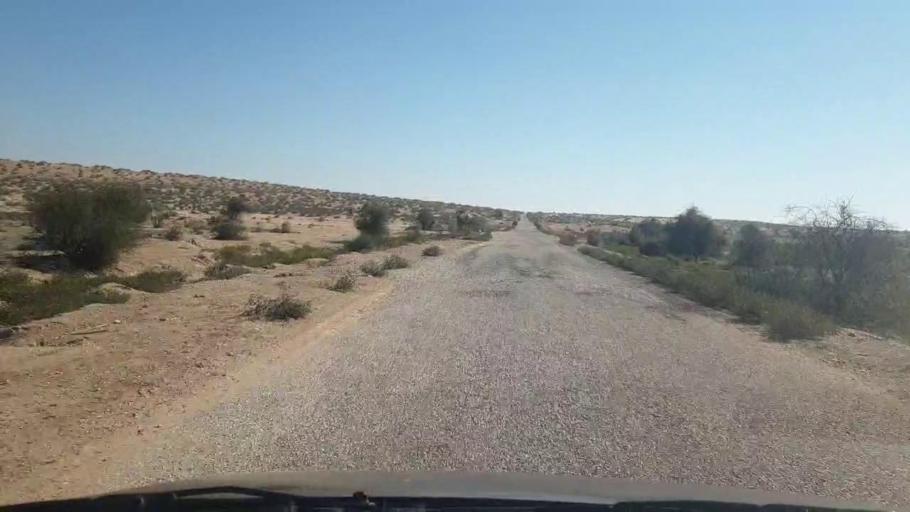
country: PK
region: Sindh
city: Bozdar
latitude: 27.0084
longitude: 68.7997
